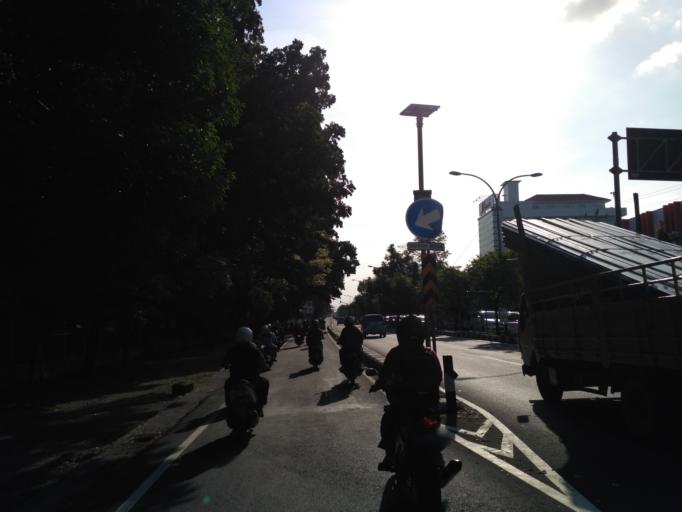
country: ID
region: Daerah Istimewa Yogyakarta
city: Depok
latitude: -7.7616
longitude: 110.4112
